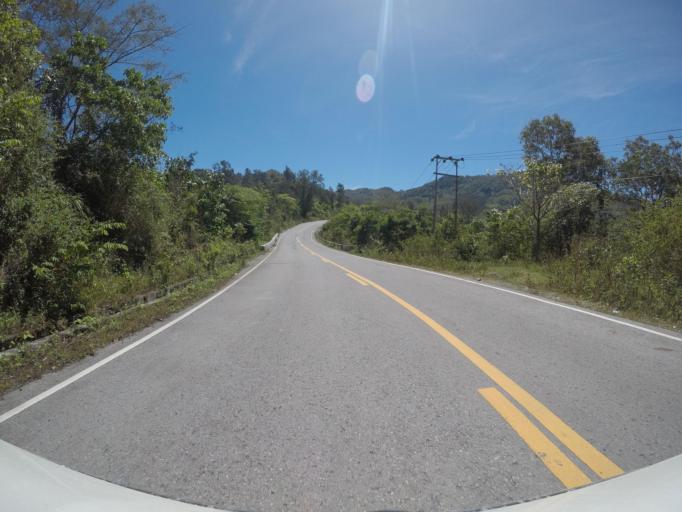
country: TL
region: Manatuto
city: Manatuto
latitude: -8.8131
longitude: 125.9735
